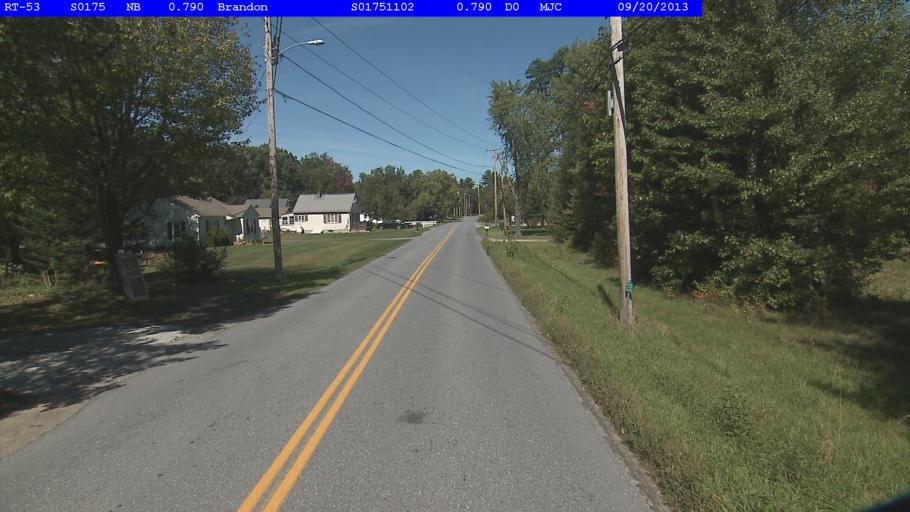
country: US
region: Vermont
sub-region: Rutland County
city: Brandon
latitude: 43.8381
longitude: -73.0562
